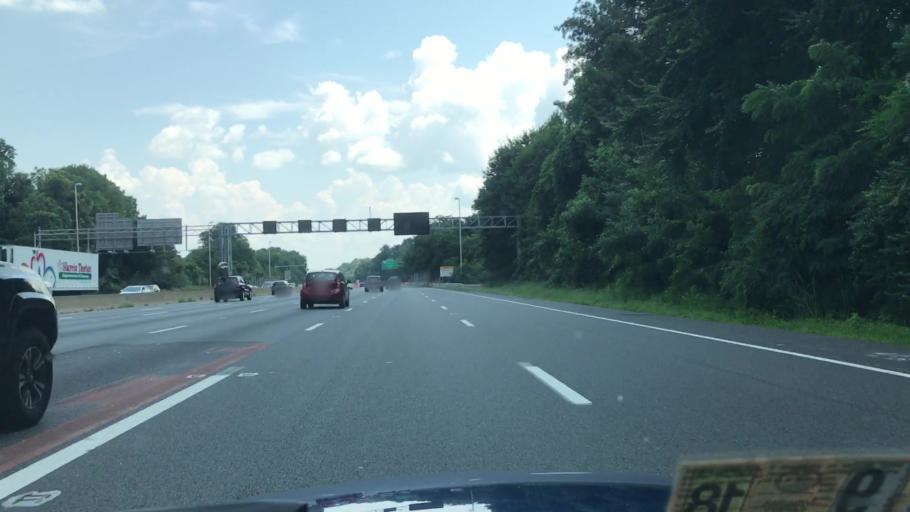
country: US
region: Virginia
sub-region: Fairfax County
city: Oakton
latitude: 38.8701
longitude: -77.3006
